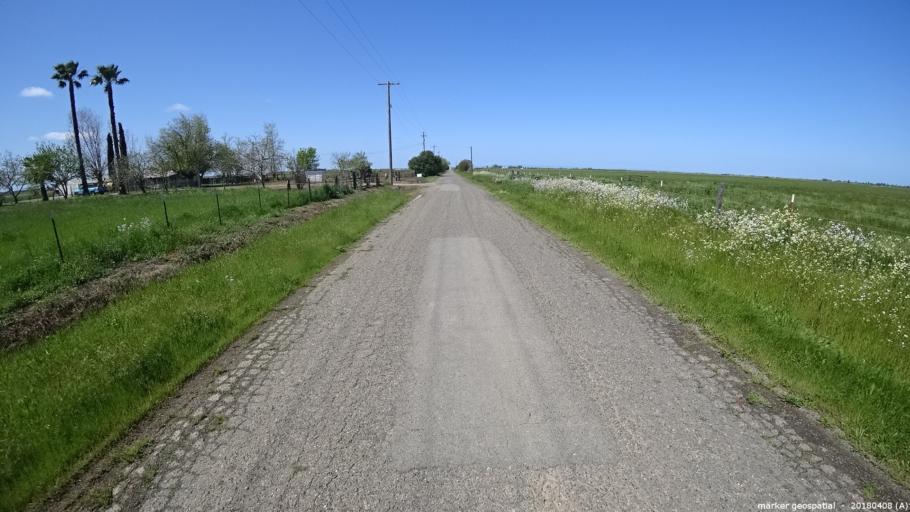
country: US
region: California
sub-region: San Joaquin County
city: Thornton
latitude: 38.2986
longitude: -121.4429
